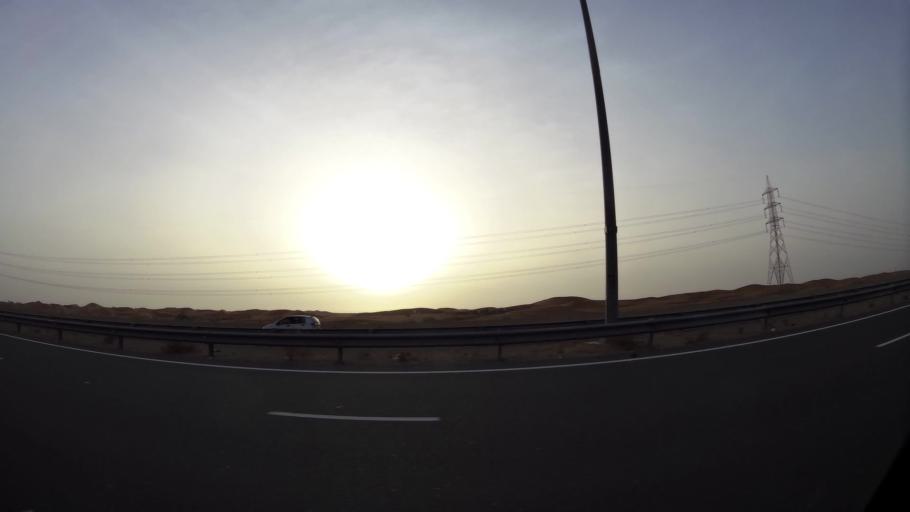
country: OM
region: Al Buraimi
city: Al Buraymi
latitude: 24.3649
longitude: 55.7910
